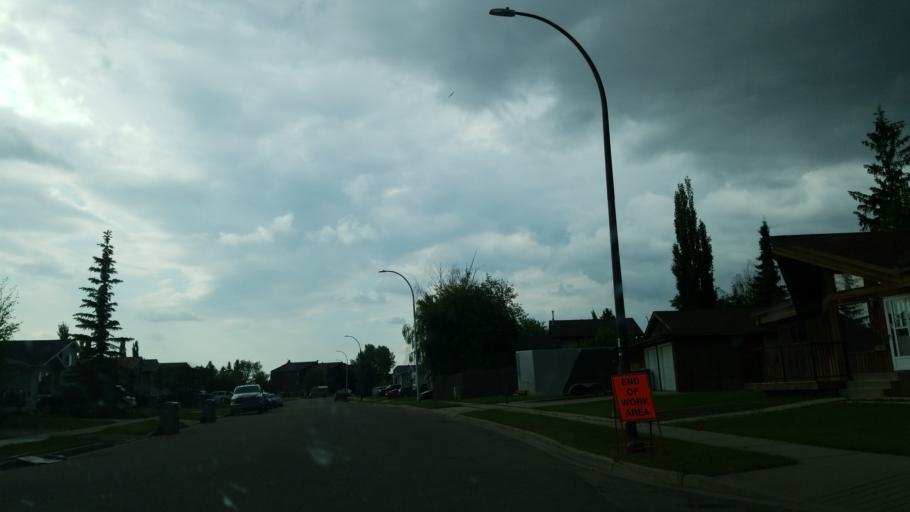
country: CA
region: Saskatchewan
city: Lloydminster
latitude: 53.2630
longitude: -110.0199
